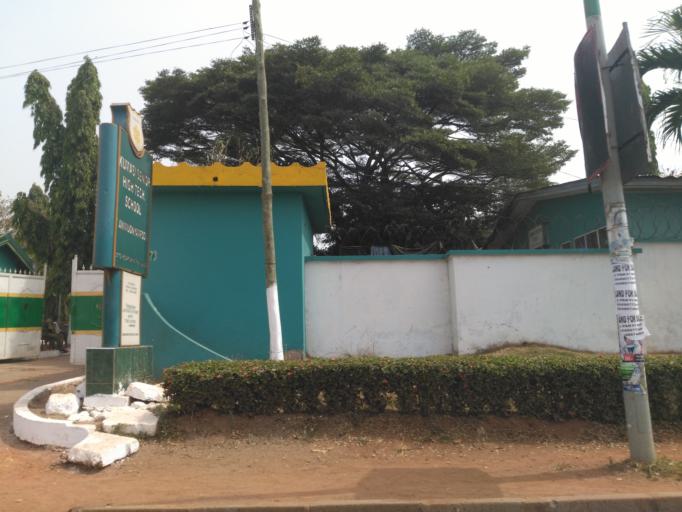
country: GH
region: Ashanti
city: Kumasi
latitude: 6.6810
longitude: -1.6440
